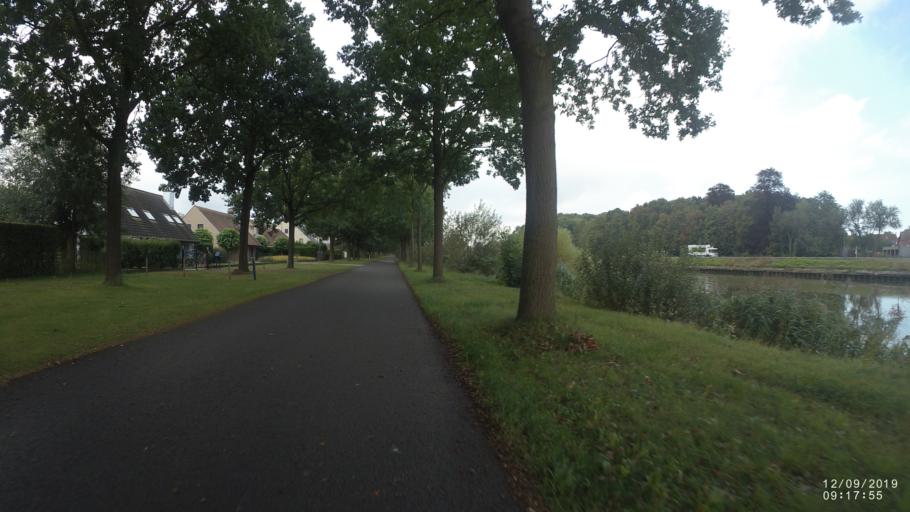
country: BE
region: Flanders
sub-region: Provincie Oost-Vlaanderen
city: Lovendegem
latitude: 51.0909
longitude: 3.6143
